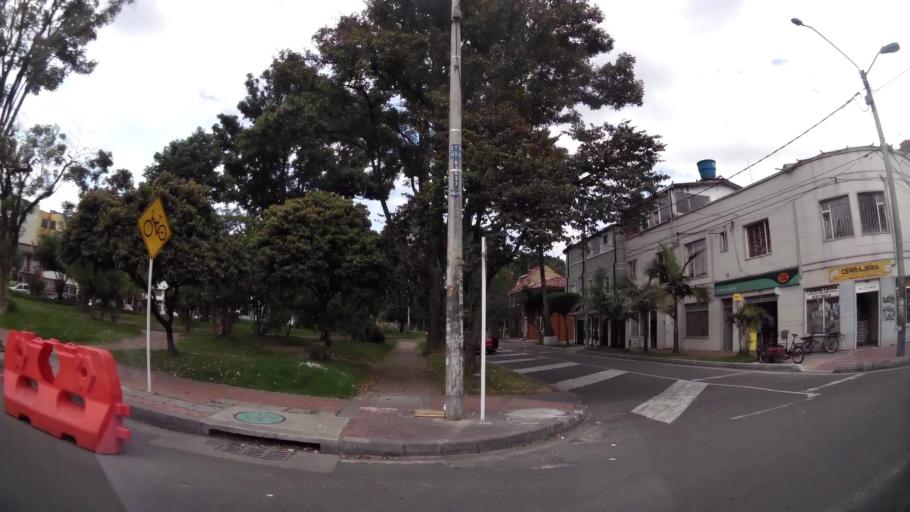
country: CO
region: Bogota D.C.
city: Bogota
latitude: 4.6316
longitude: -74.0723
